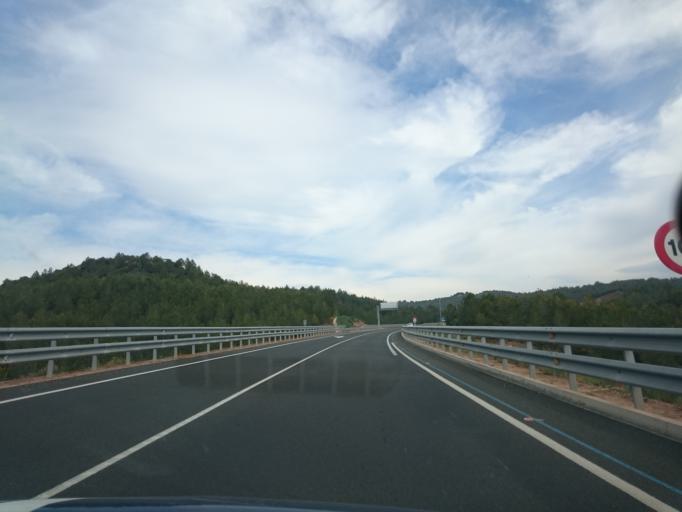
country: ES
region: Catalonia
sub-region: Provincia de Barcelona
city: Sant Salvador de Guardiola
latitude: 41.6992
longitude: 1.7793
